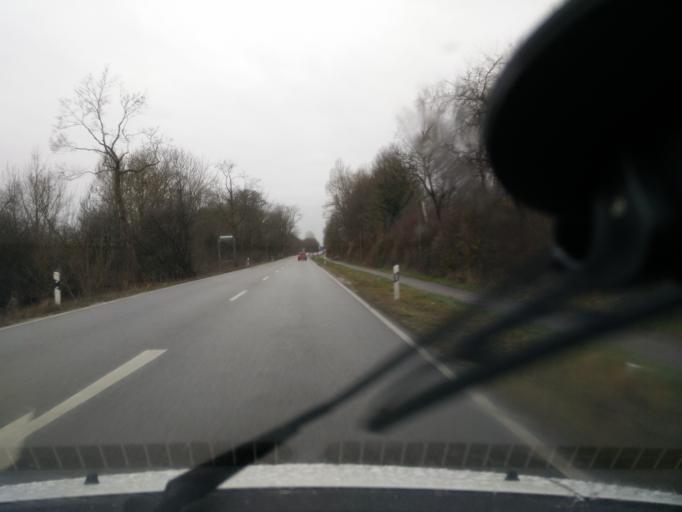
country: DE
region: Bavaria
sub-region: Upper Bavaria
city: Oberschleissheim
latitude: 48.2514
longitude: 11.5445
